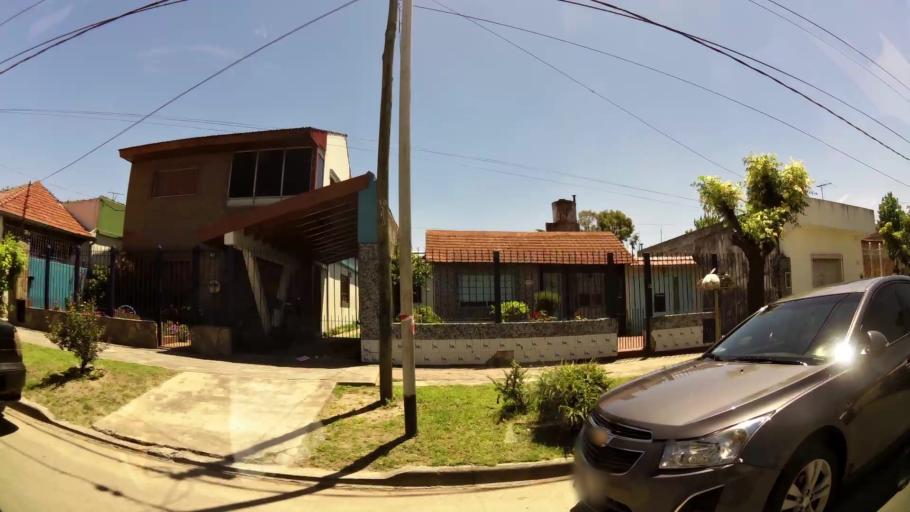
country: AR
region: Buenos Aires
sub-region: Partido de Quilmes
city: Quilmes
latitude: -34.7175
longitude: -58.3233
